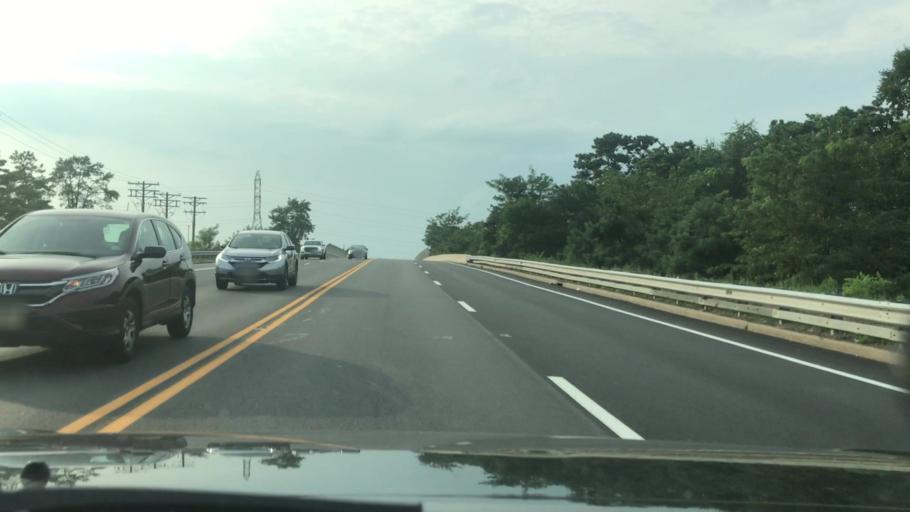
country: US
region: New Jersey
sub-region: Ocean County
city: Leisure Village
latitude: 40.0643
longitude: -74.1602
